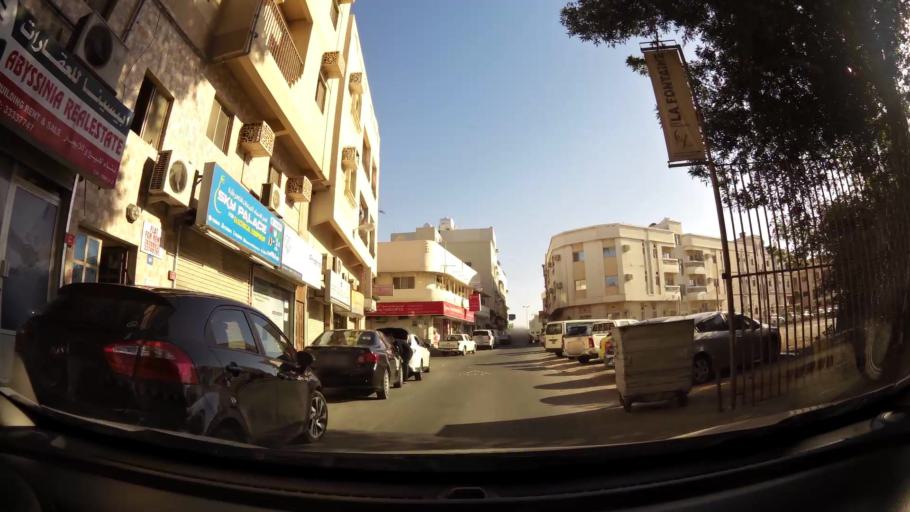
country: BH
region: Manama
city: Manama
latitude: 26.2326
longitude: 50.5858
